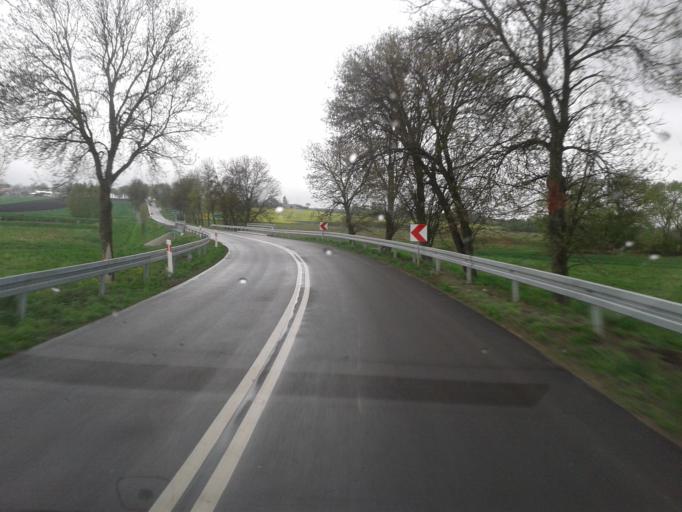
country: PL
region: Lublin Voivodeship
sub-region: Powiat tomaszowski
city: Telatyn
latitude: 50.4929
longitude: 23.8769
